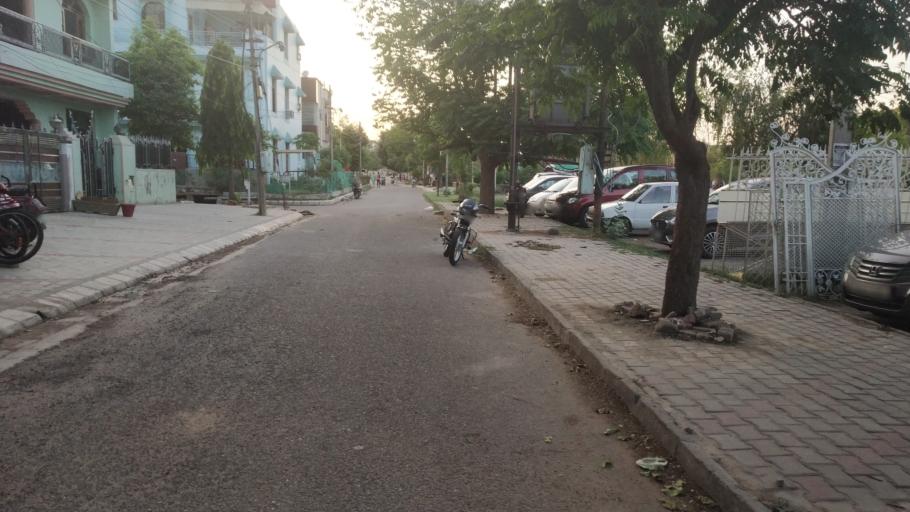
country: IN
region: Punjab
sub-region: Ajitgarh
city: Mohali
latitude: 30.6862
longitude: 76.7303
